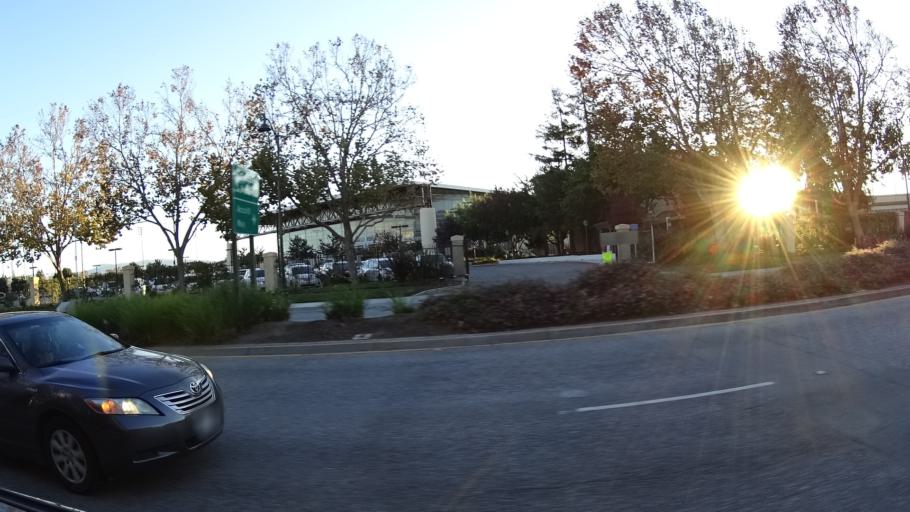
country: US
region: California
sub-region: Santa Clara County
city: Santa Clara
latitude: 37.3504
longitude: -121.9343
